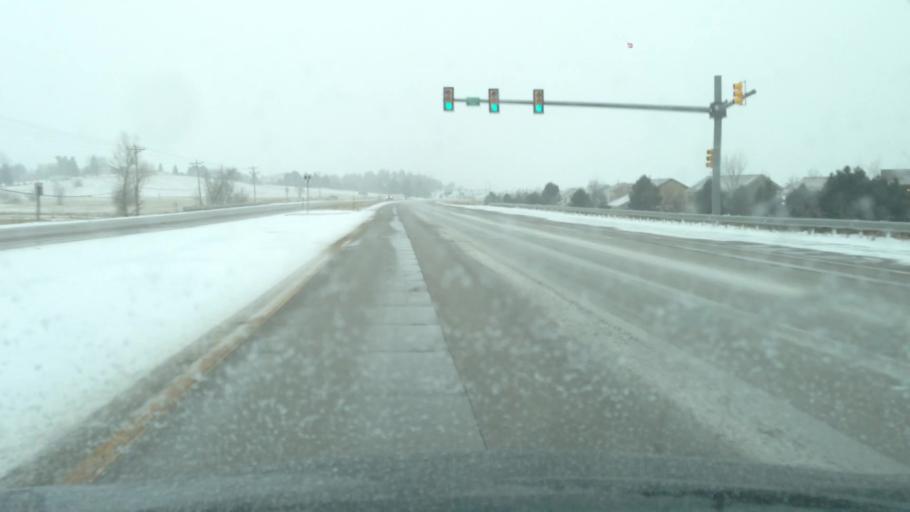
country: US
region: Colorado
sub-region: Arapahoe County
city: Dove Valley
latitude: 39.5848
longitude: -104.7961
